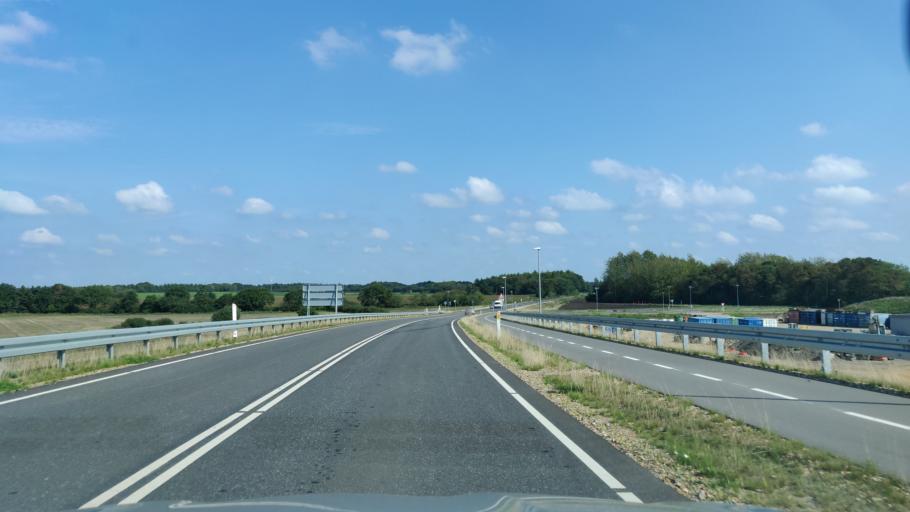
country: DK
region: Central Jutland
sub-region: Herning Kommune
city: Avlum
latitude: 56.2205
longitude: 8.8521
